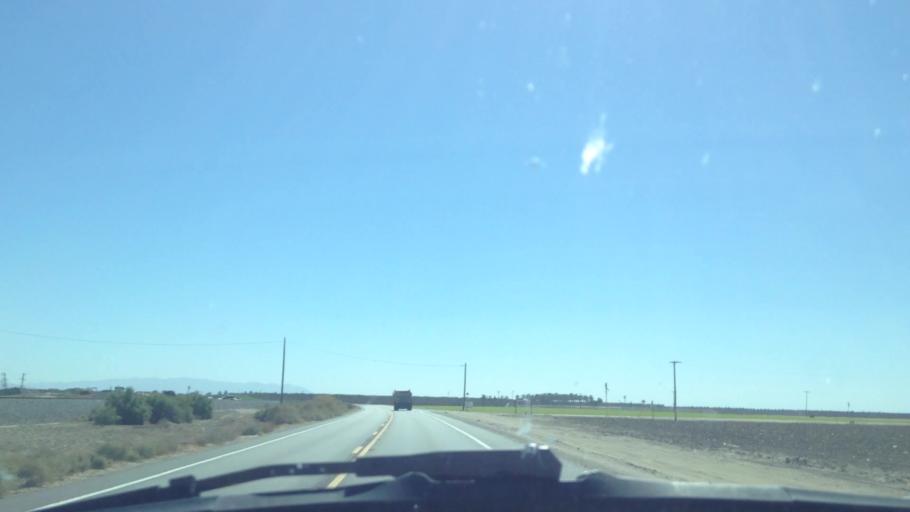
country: US
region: California
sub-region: Riverside County
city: Mecca
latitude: 33.5394
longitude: -116.0280
